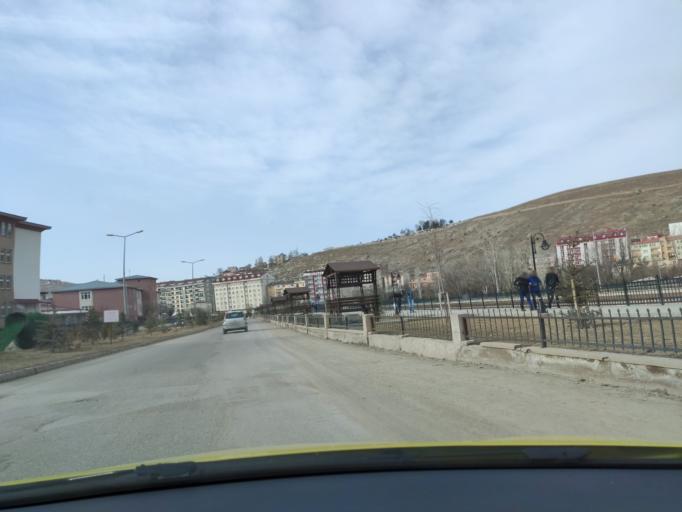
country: TR
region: Bayburt
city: Bayburt
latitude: 40.2497
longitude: 40.2322
